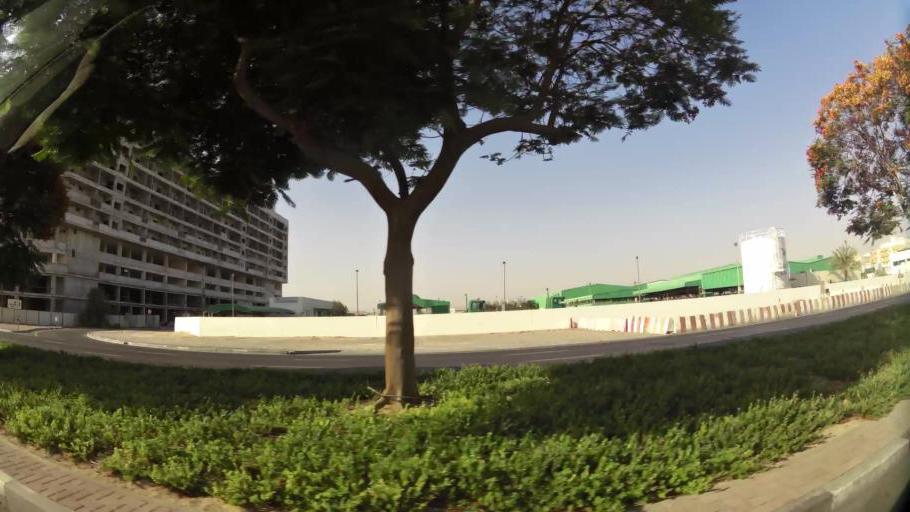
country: AE
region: Ash Shariqah
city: Sharjah
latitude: 25.2795
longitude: 55.3815
